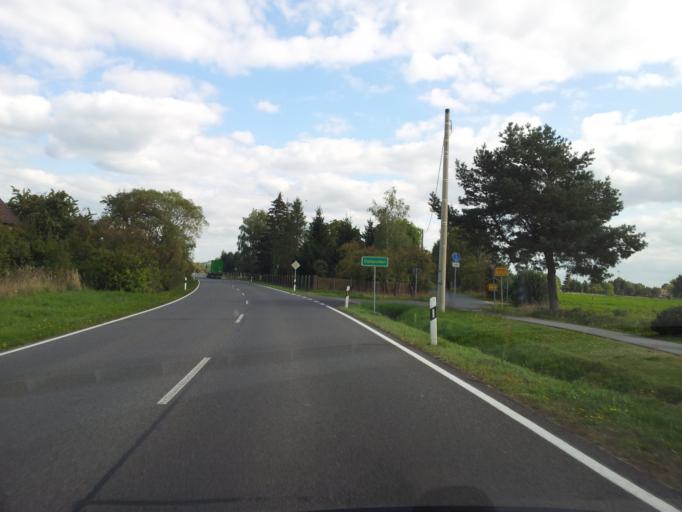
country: DE
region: Brandenburg
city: Sallgast
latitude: 51.6113
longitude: 13.8504
